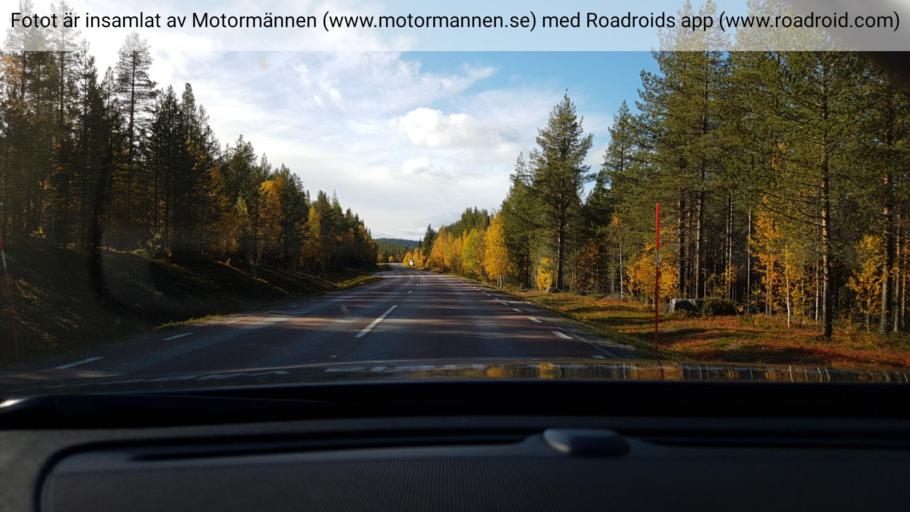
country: SE
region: Norrbotten
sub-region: Arjeplogs Kommun
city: Arjeplog
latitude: 66.0584
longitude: 17.9371
